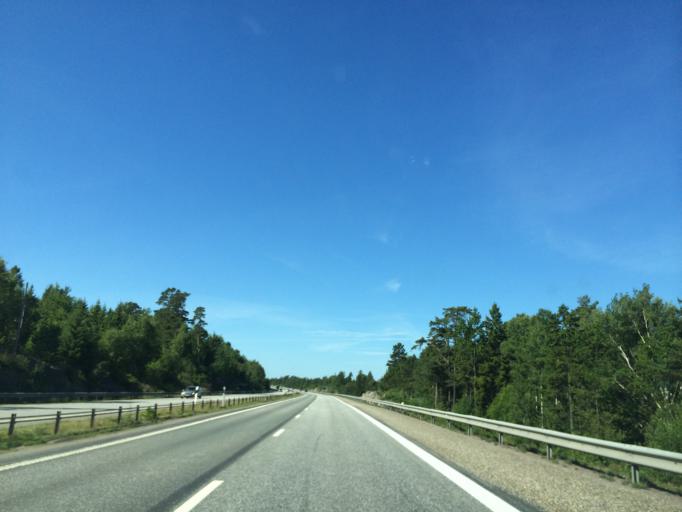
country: SE
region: Joenkoeping
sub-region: Jonkopings Kommun
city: Graenna
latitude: 57.9676
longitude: 14.3661
